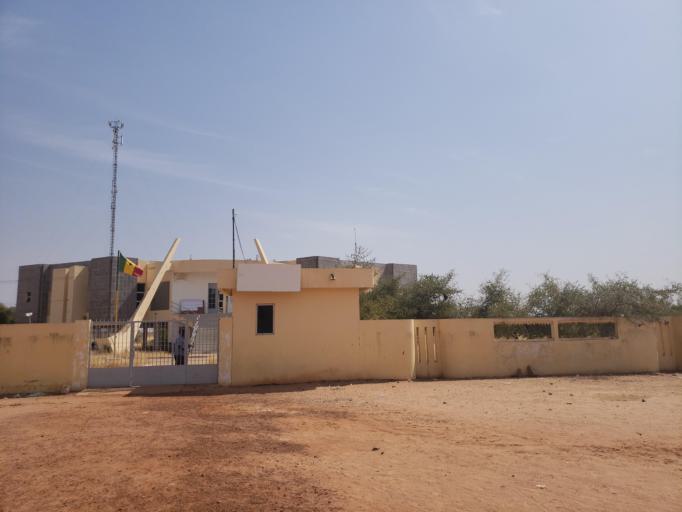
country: SN
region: Matam
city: Ranerou
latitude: 15.2988
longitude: -13.9563
